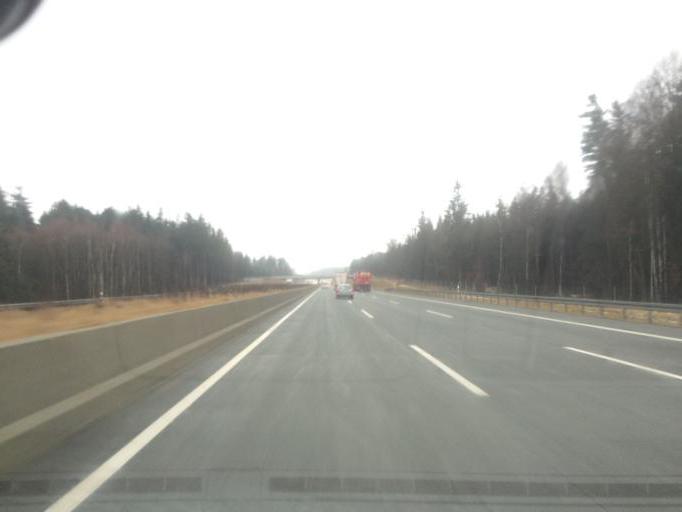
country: DE
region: Thuringia
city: Dittersdorf
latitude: 50.6341
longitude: 11.7970
